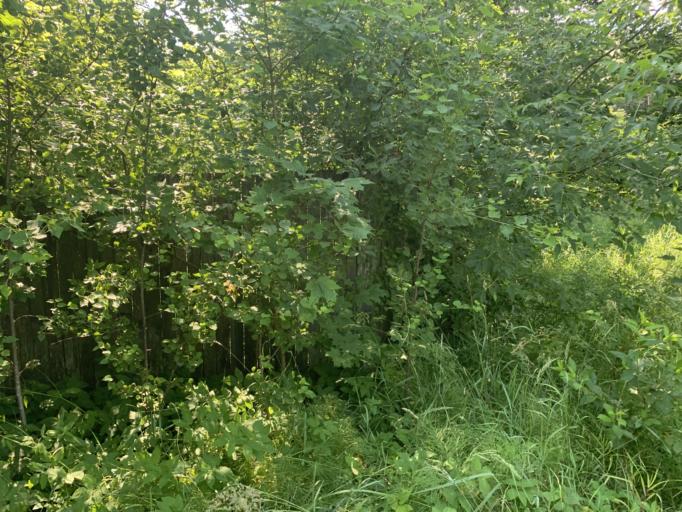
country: RU
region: Moskovskaya
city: Mamontovka
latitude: 55.9710
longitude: 37.8059
